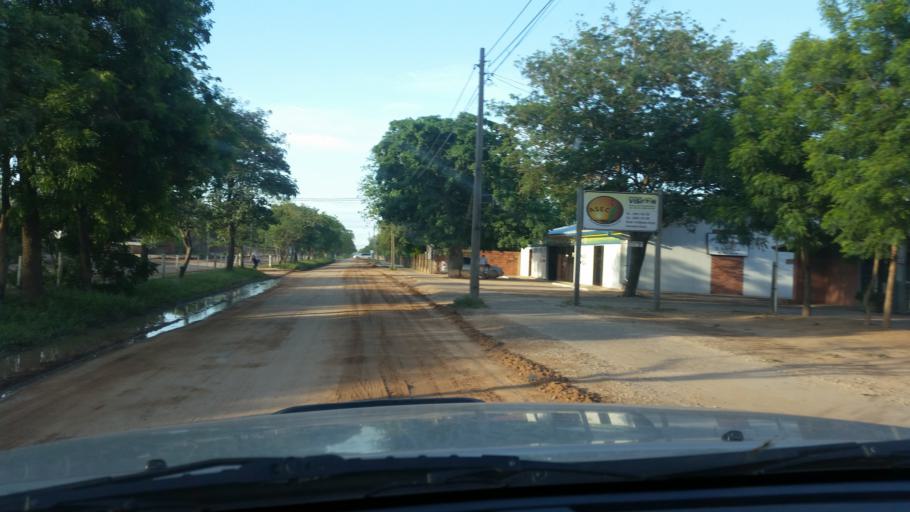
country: PY
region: Boqueron
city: Filadelfia
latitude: -22.3558
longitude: -60.0309
